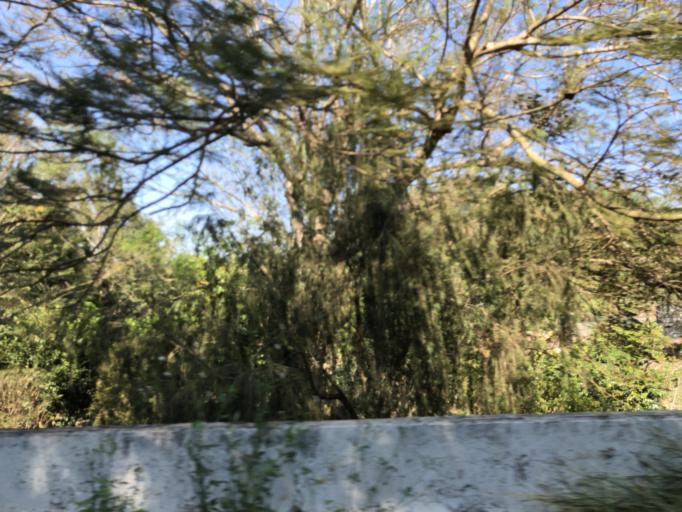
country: TW
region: Taiwan
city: Yujing
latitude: 23.0528
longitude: 120.3797
